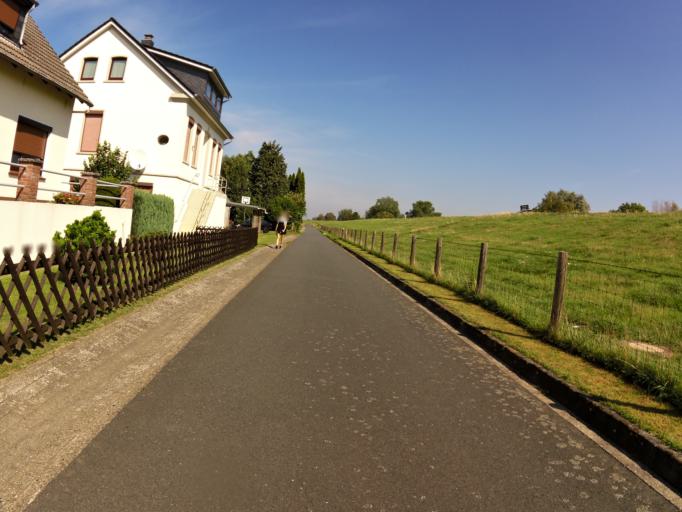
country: DE
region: Lower Saxony
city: Elsfleth
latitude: 53.2626
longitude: 8.4783
